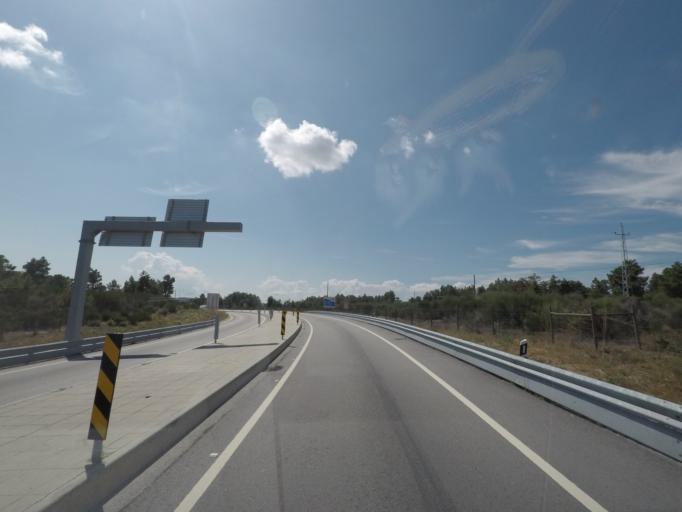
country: PT
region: Vila Real
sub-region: Murca
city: Murca
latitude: 41.3399
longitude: -7.4700
